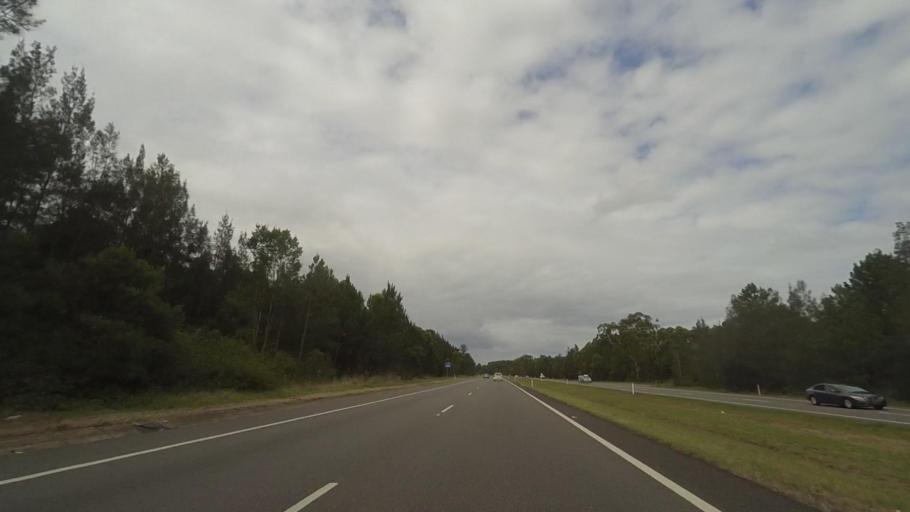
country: AU
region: New South Wales
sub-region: Port Stephens Shire
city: Raymond Terrace
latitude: -32.7738
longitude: 151.7579
